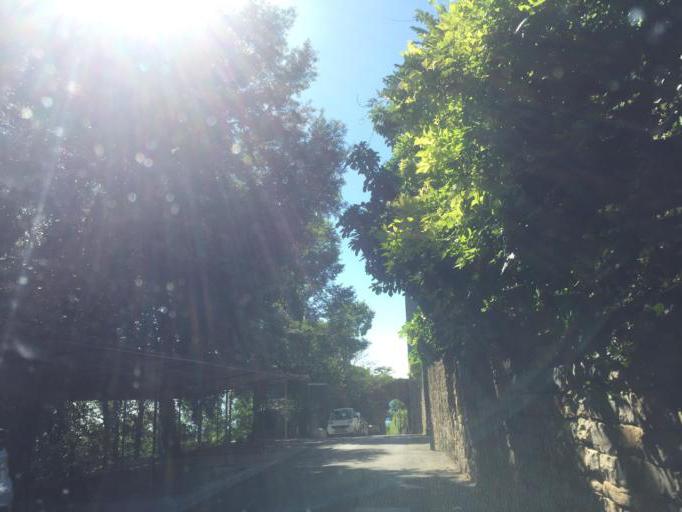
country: SI
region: Piran-Pirano
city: Piran
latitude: 45.5267
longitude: 13.5713
